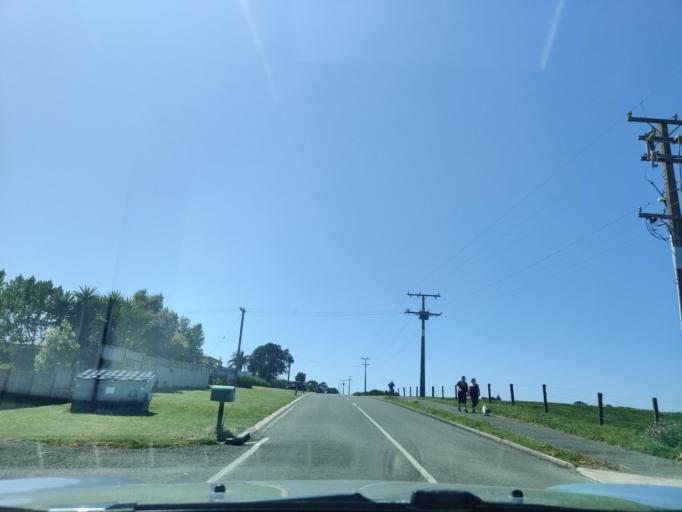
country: NZ
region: Taranaki
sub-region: South Taranaki District
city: Hawera
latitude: -39.5999
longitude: 174.2633
